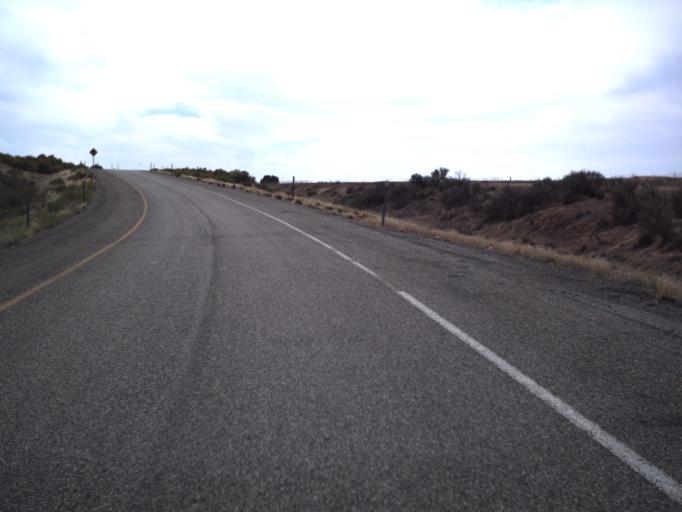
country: US
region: Colorado
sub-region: Mesa County
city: Loma
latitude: 39.1743
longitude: -109.1288
